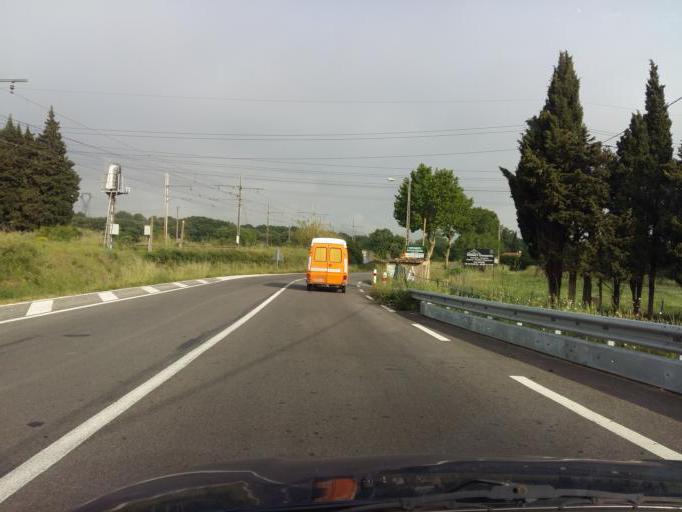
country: FR
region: Languedoc-Roussillon
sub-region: Departement du Gard
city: Saint-Genies-de-Comolas
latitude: 44.0898
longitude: 4.7049
